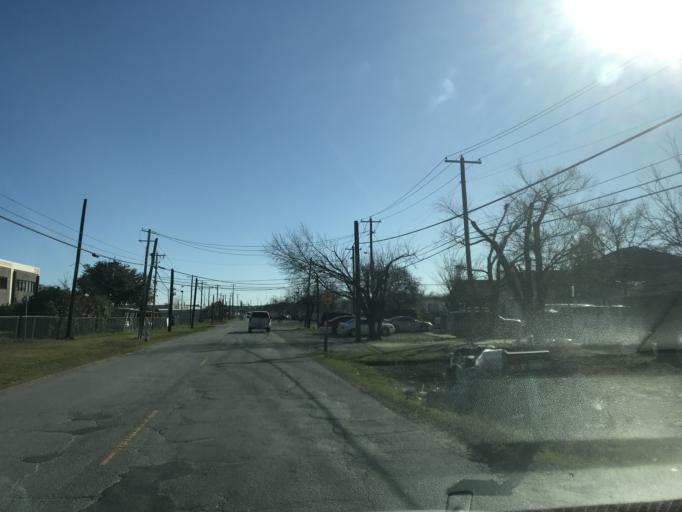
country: US
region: Texas
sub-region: Dallas County
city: Cockrell Hill
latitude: 32.7743
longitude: -96.9043
